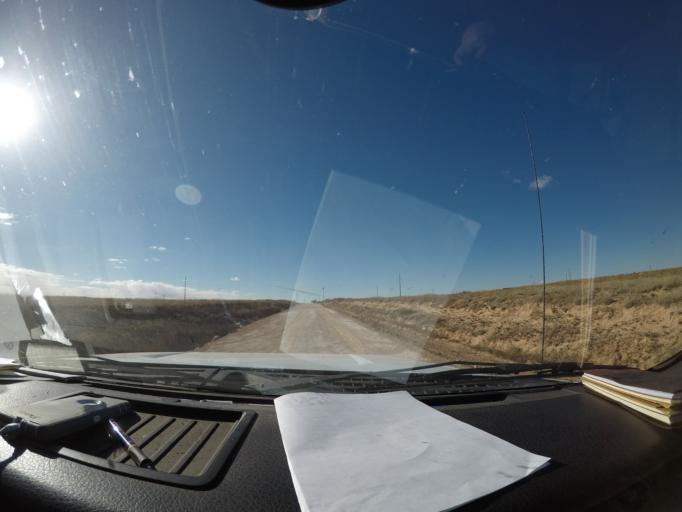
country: US
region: New Mexico
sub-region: Curry County
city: Clovis
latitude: 34.5797
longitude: -103.1391
